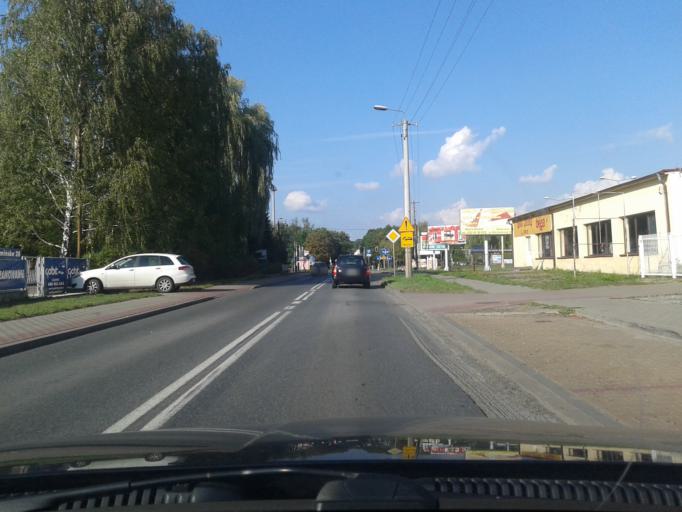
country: PL
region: Silesian Voivodeship
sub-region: Powiat wodzislawski
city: Wodzislaw Slaski
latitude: 49.9957
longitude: 18.4579
